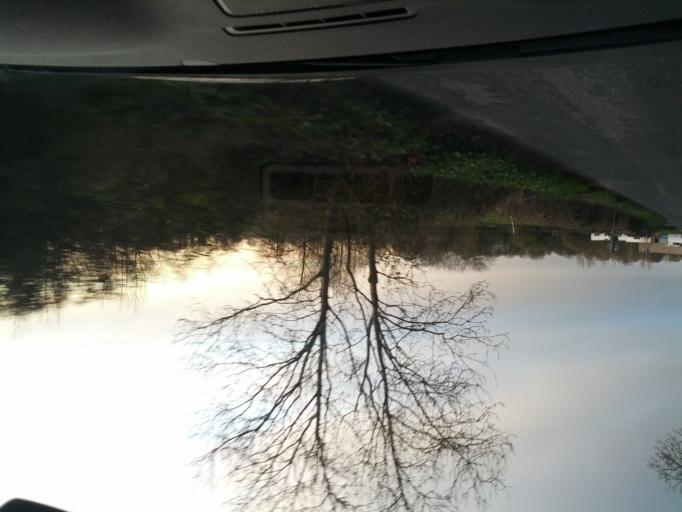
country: IE
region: Munster
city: Nenagh Bridge
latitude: 52.8847
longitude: -8.1960
